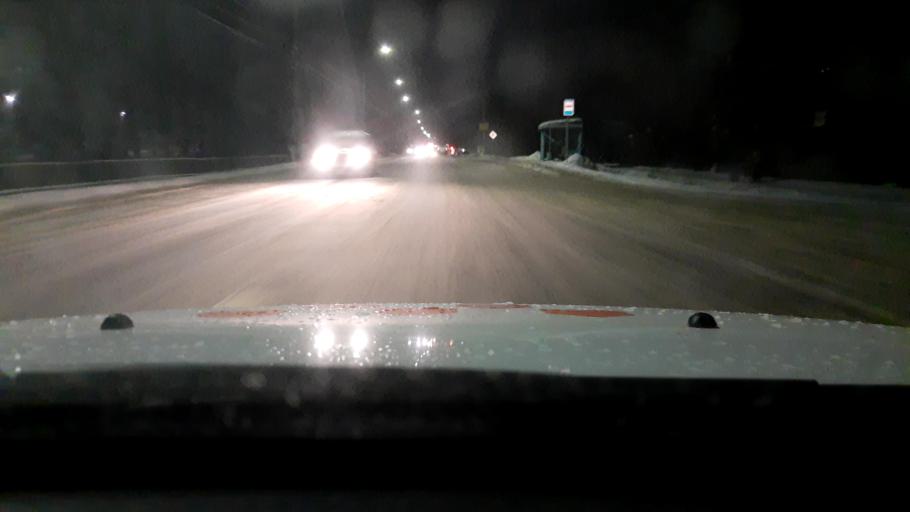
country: RU
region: Nizjnij Novgorod
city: Gorodets
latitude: 56.6700
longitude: 43.4669
